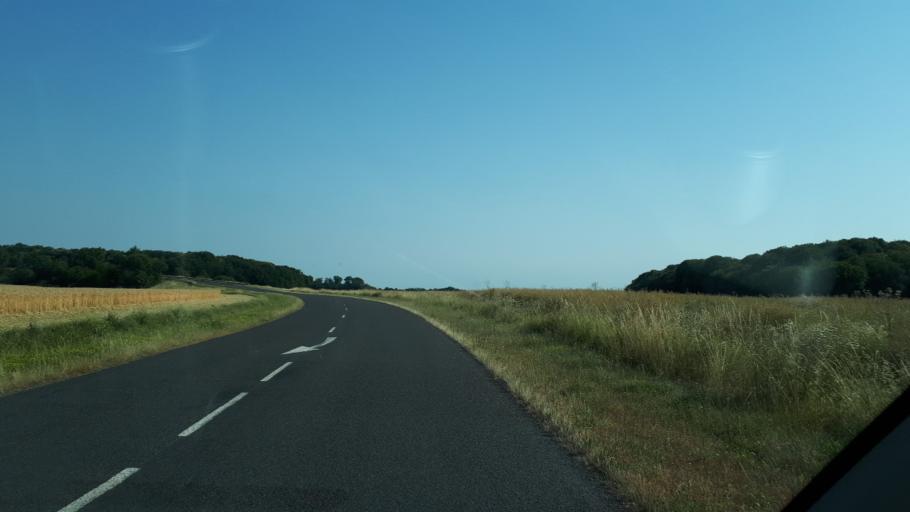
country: FR
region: Centre
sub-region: Departement du Loir-et-Cher
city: La Ville-aux-Clercs
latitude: 47.9729
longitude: 1.0471
